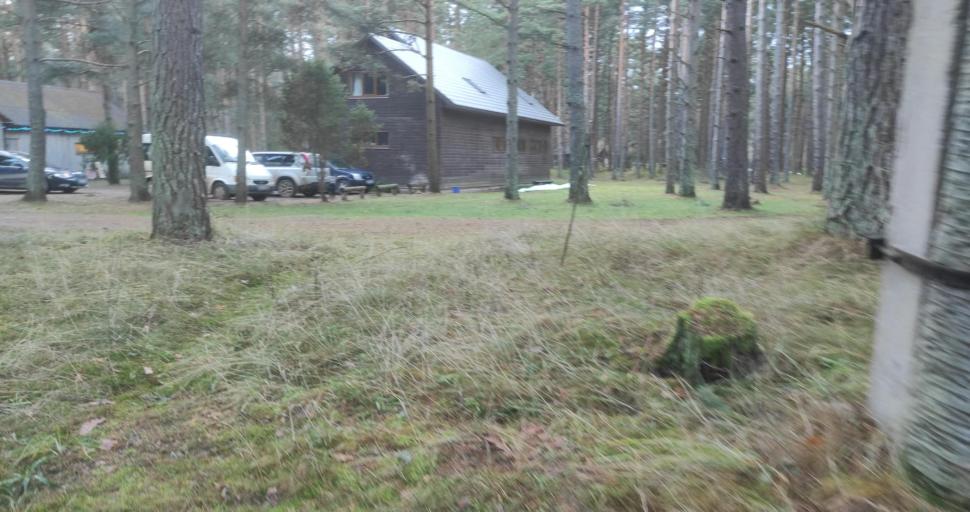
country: LV
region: Pavilostas
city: Pavilosta
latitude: 56.7814
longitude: 21.0658
